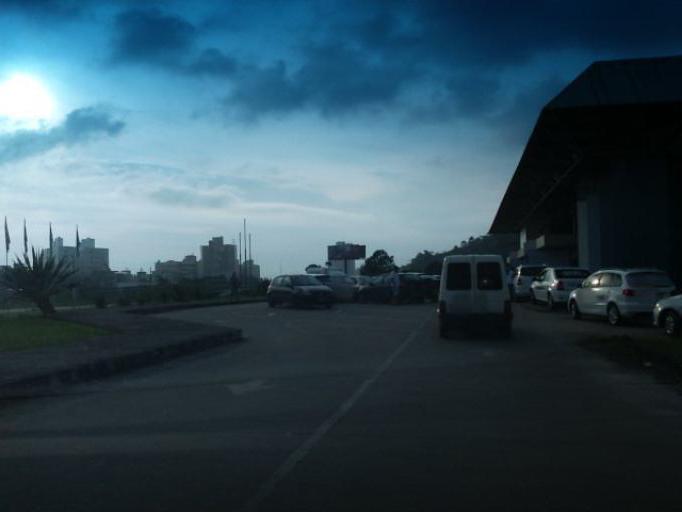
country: BR
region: Santa Catarina
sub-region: Itapema
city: Itapema
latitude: -27.1045
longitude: -48.6174
